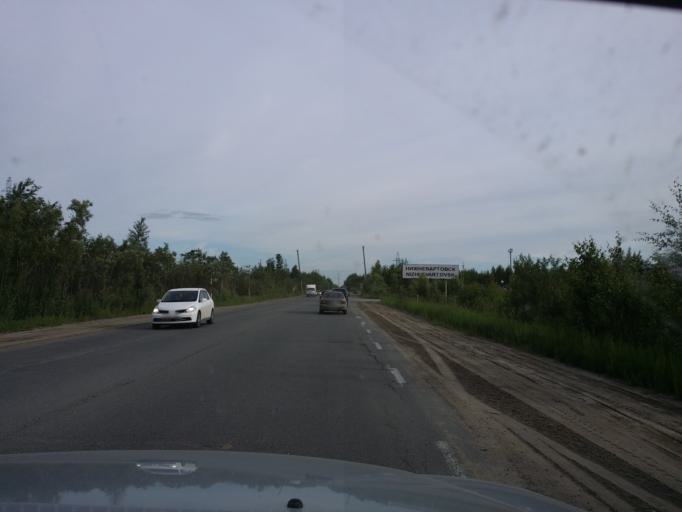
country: RU
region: Khanty-Mansiyskiy Avtonomnyy Okrug
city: Nizhnevartovsk
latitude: 60.9578
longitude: 76.6635
